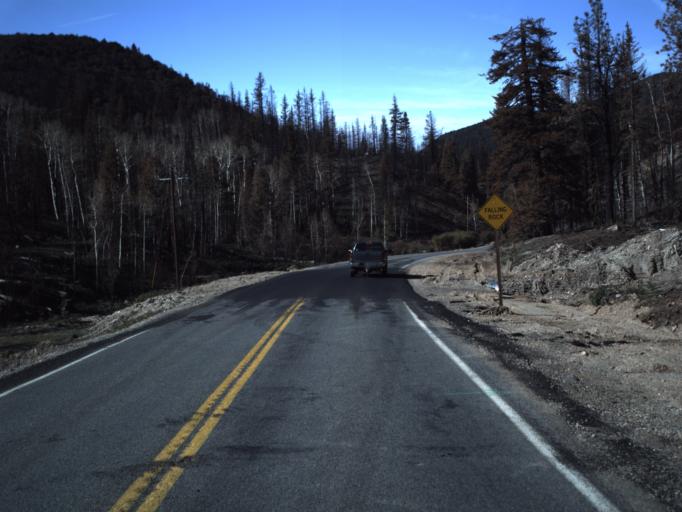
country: US
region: Utah
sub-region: Iron County
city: Parowan
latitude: 37.7438
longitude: -112.8380
